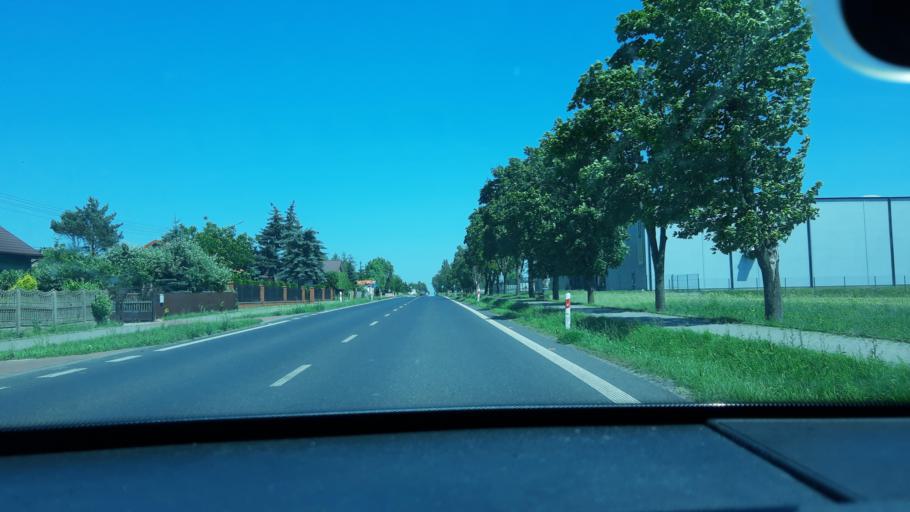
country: PL
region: Lodz Voivodeship
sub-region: Powiat zdunskowolski
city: Zapolice
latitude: 51.6058
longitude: 18.8591
